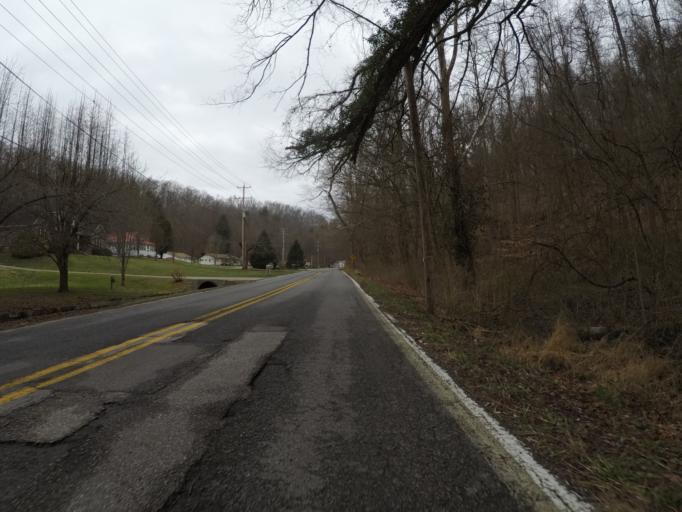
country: US
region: West Virginia
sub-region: Cabell County
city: Barboursville
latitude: 38.4498
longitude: -82.3003
